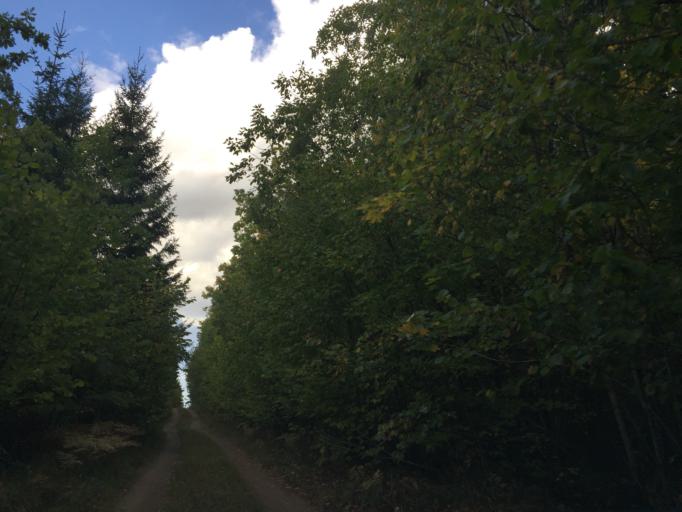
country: LV
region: Ligatne
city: Ligatne
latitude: 57.1160
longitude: 25.1365
